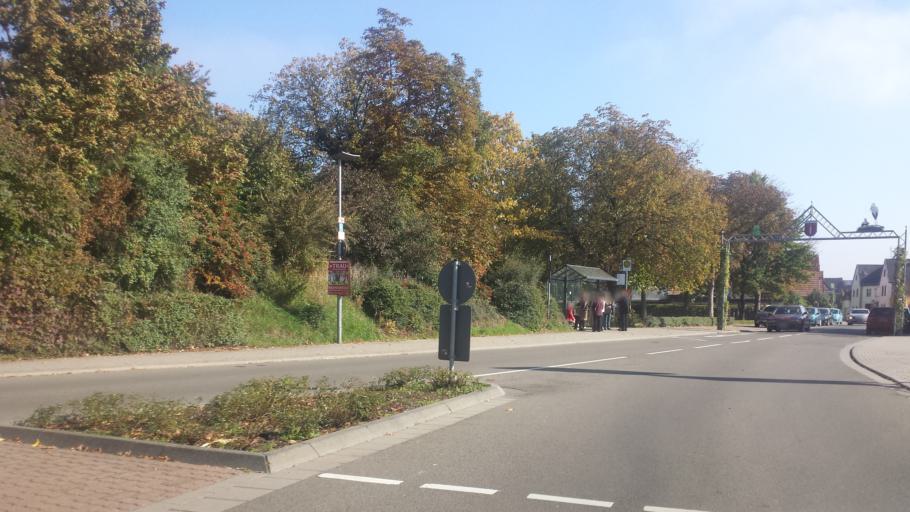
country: DE
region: Rheinland-Pfalz
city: Offenbach an der Queich
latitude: 49.1946
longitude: 8.1869
